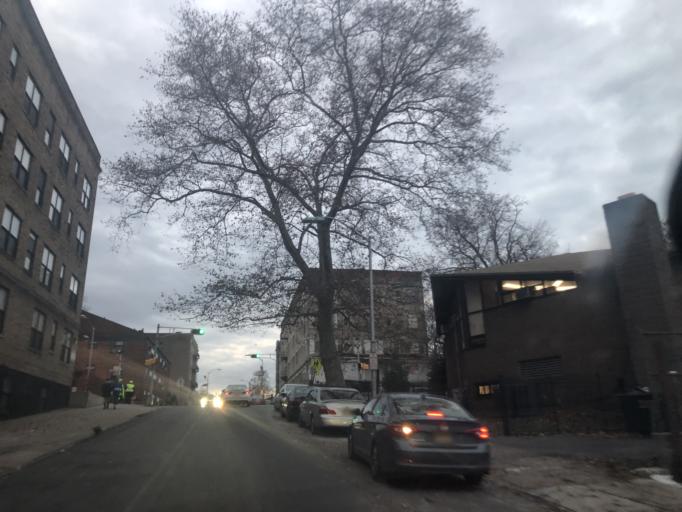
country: US
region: New Jersey
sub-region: Essex County
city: East Orange
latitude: 40.7637
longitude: -74.2082
